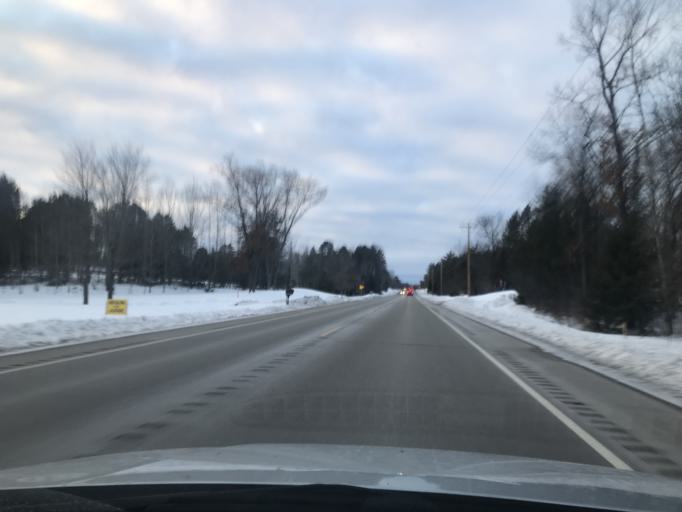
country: US
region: Wisconsin
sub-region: Marinette County
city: Marinette
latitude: 45.1562
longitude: -87.7135
